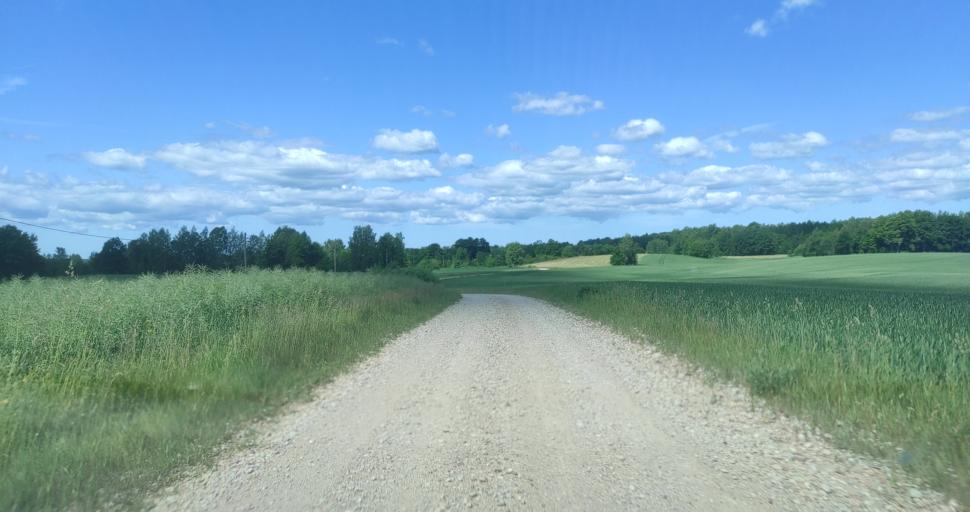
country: LV
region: Alsunga
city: Alsunga
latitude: 56.8767
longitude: 21.7172
